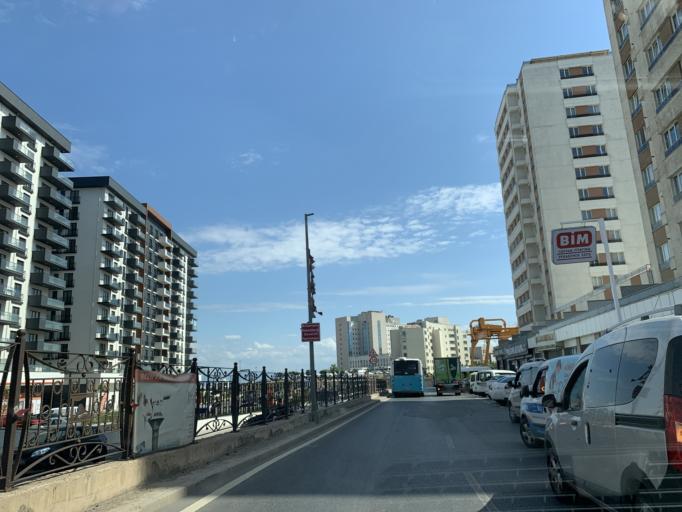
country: TR
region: Istanbul
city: Pendik
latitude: 40.8906
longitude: 29.2630
